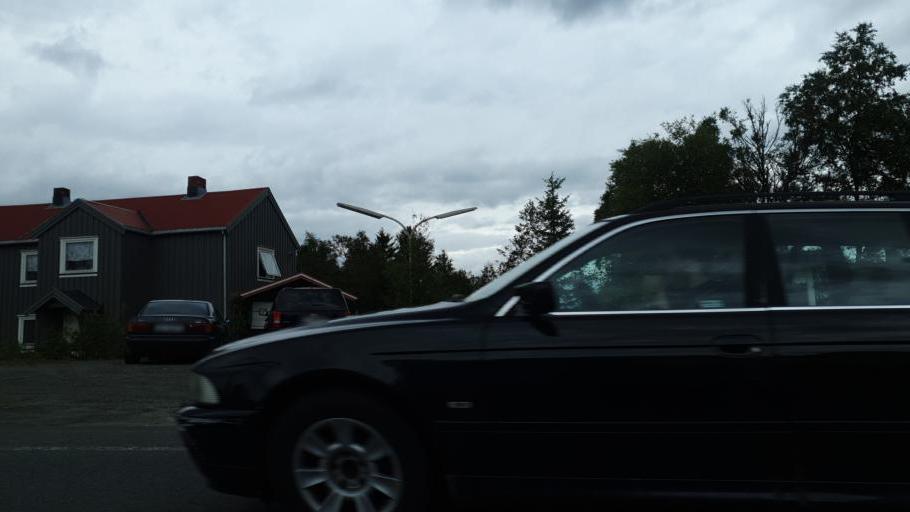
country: NO
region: Sor-Trondelag
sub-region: Rennebu
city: Berkak
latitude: 62.8263
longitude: 10.0079
